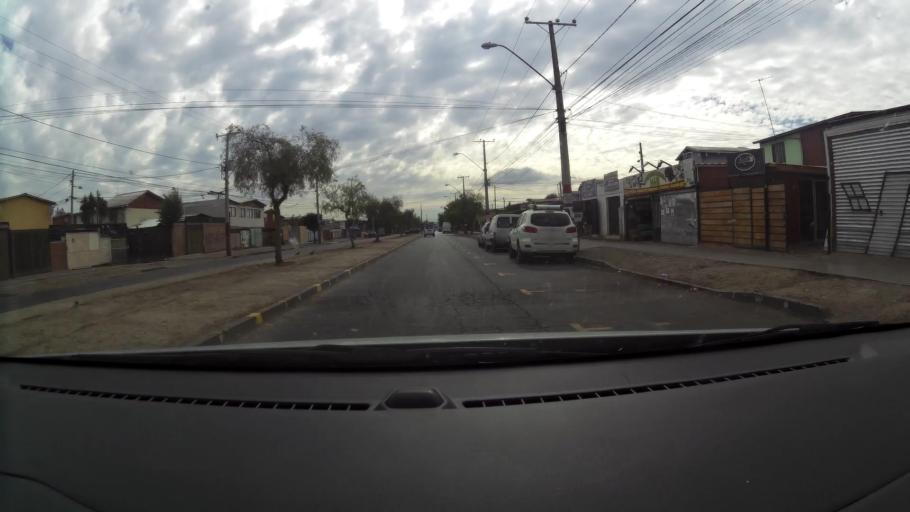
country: CL
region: Santiago Metropolitan
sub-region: Provincia de Cordillera
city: Puente Alto
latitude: -33.6213
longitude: -70.6133
